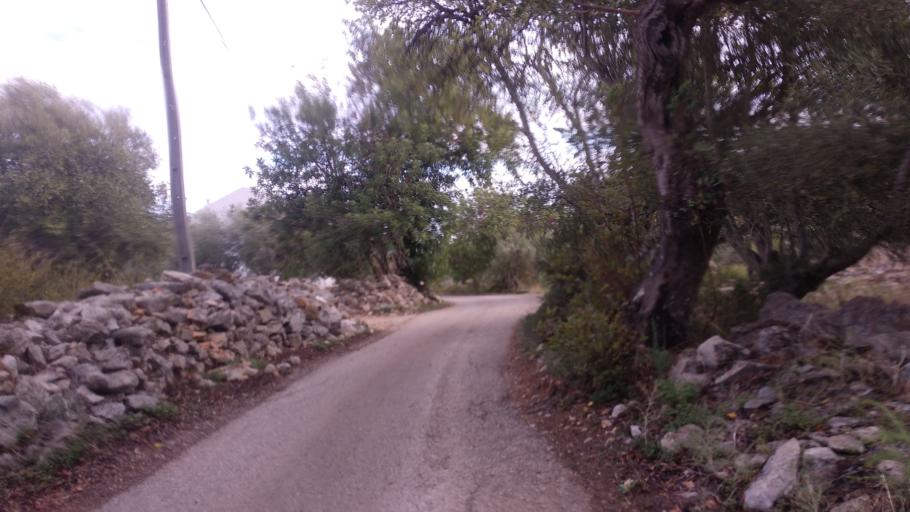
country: PT
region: Faro
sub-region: Sao Bras de Alportel
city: Sao Bras de Alportel
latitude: 37.1571
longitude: -7.8987
